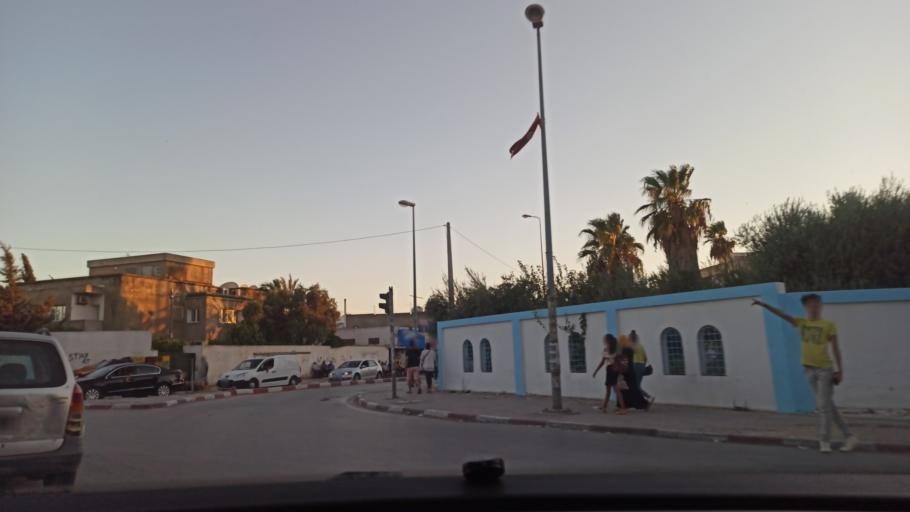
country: TN
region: Ariana
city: Ariana
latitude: 36.8646
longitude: 10.2001
